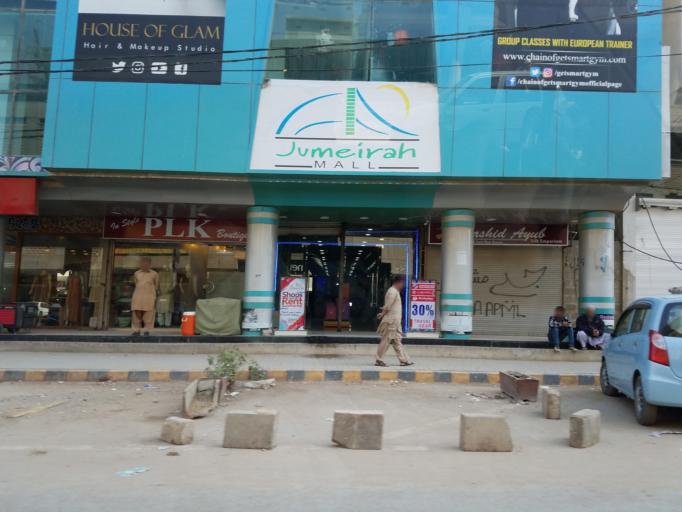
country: PK
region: Sindh
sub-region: Karachi District
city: Karachi
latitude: 24.8767
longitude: 67.0631
